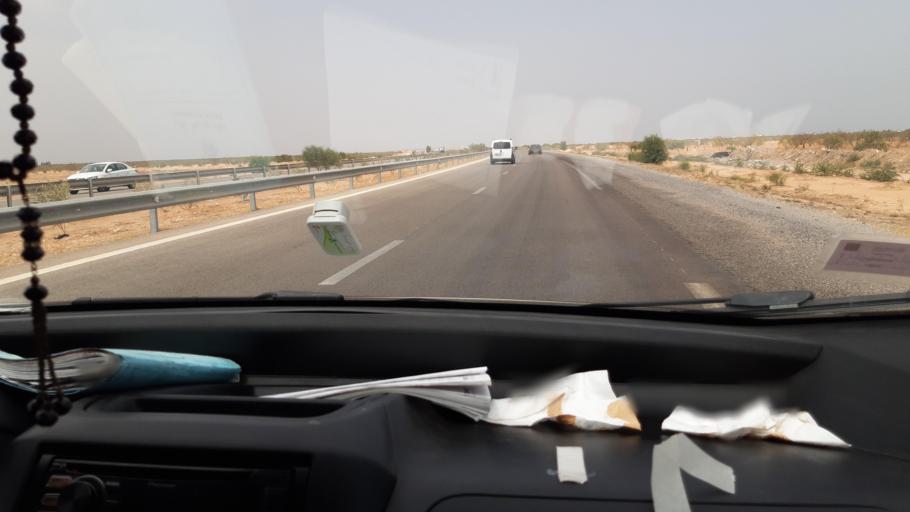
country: TN
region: Safaqis
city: Sfax
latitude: 34.8455
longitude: 10.6744
